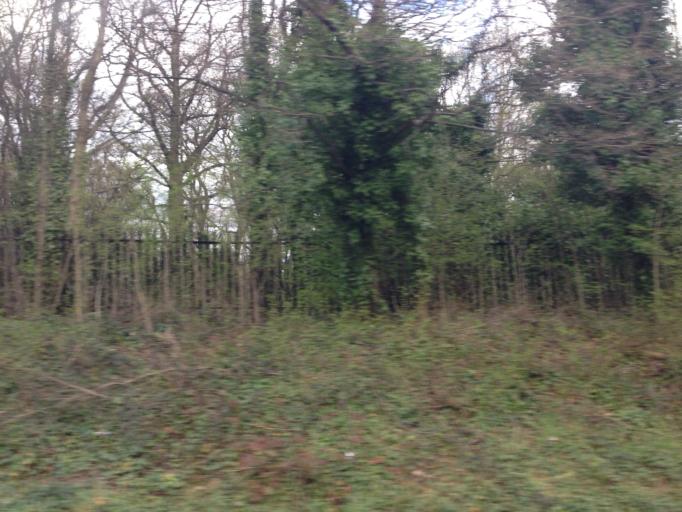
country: GB
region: England
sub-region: Greater London
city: Brixton Hill
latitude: 51.4307
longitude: -0.1385
